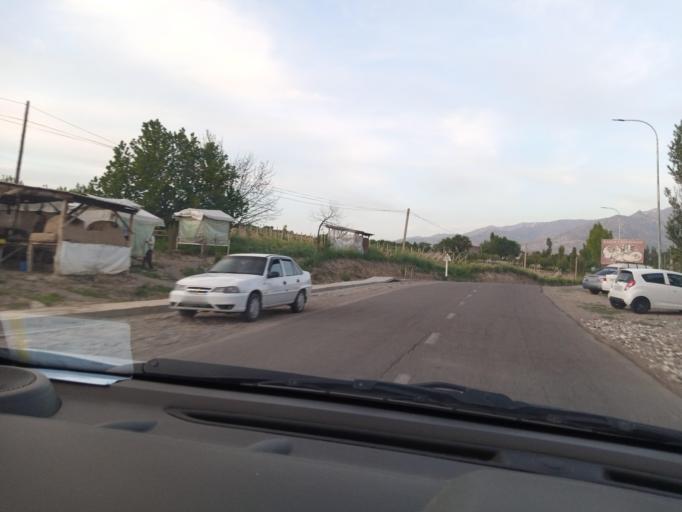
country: UZ
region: Toshkent
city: Parkent
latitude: 41.2456
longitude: 69.7362
